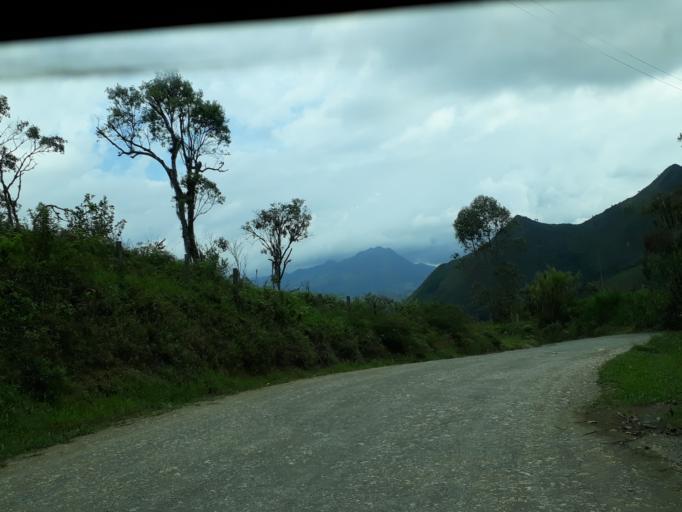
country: CO
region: Cundinamarca
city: Pacho
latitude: 5.2199
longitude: -74.1906
